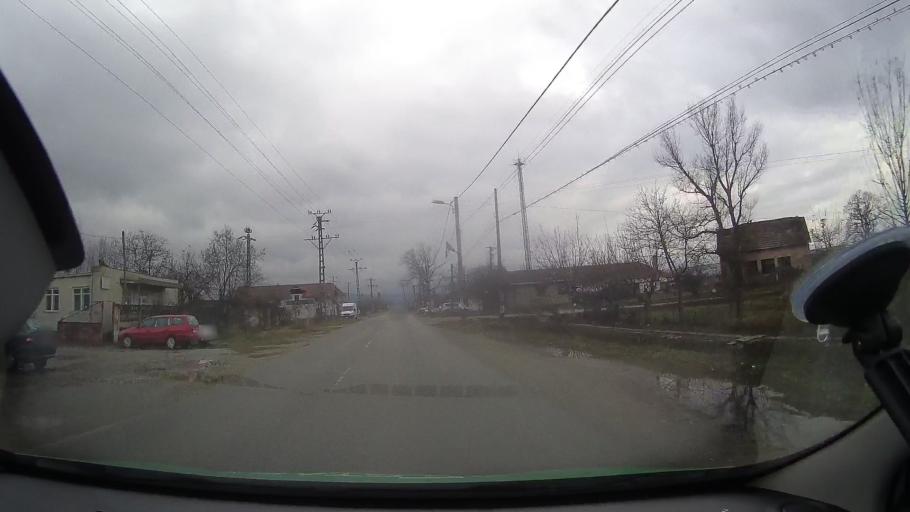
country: RO
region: Arad
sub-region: Comuna Sebis
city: Sebis
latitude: 46.3633
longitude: 22.1308
